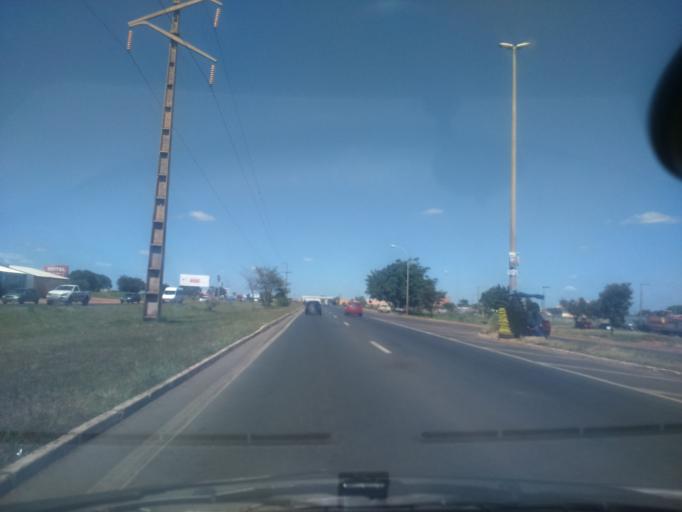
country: BR
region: Goias
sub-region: Luziania
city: Luziania
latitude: -16.0445
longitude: -48.0419
